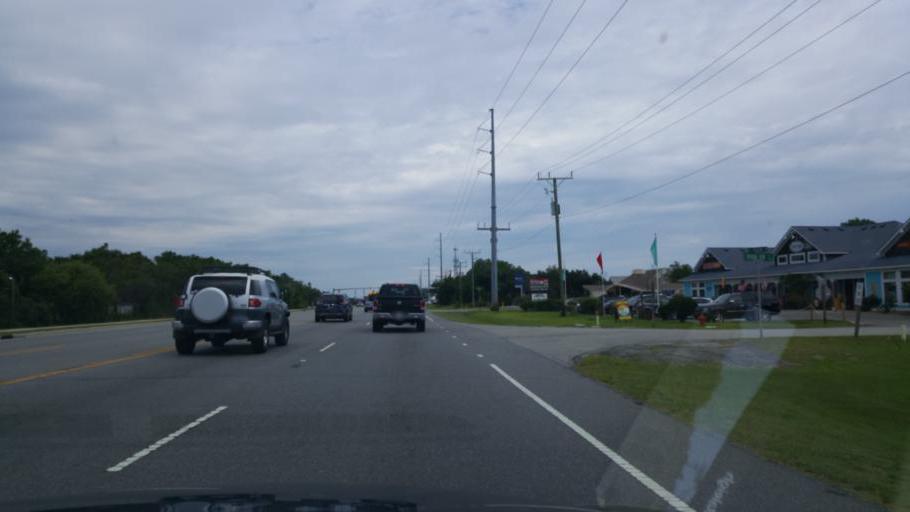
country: US
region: North Carolina
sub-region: Dare County
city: Nags Head
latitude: 35.9814
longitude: -75.6426
